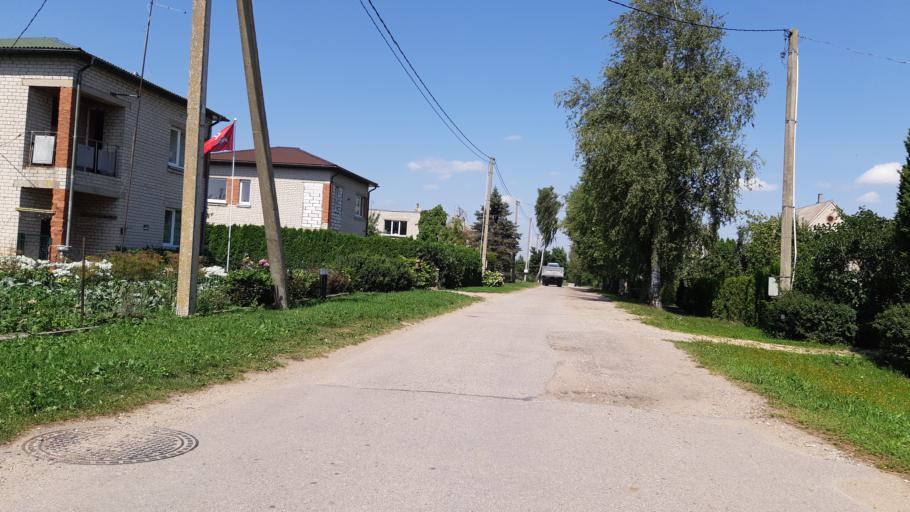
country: LT
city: Virbalis
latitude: 54.6210
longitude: 22.8165
